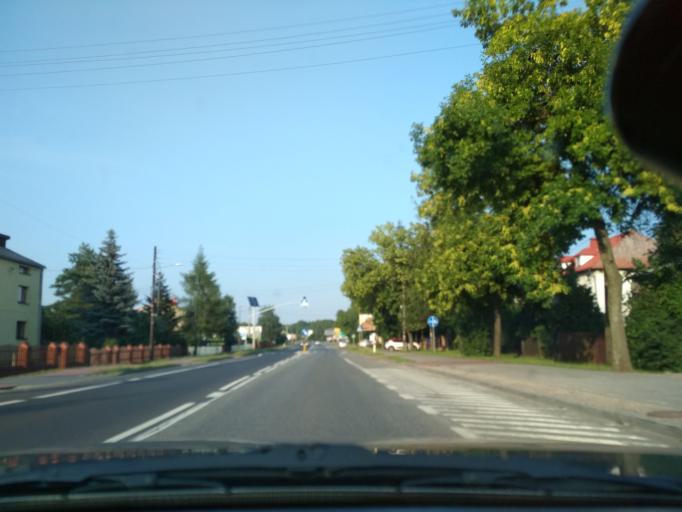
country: PL
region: Silesian Voivodeship
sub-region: Powiat zawiercianski
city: Zawiercie
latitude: 50.4773
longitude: 19.4691
